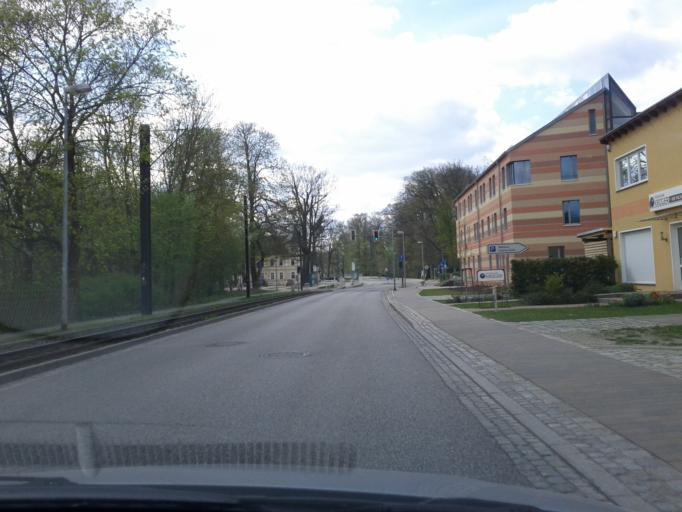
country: DE
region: Brandenburg
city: Schoneiche
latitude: 52.4786
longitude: 13.7021
